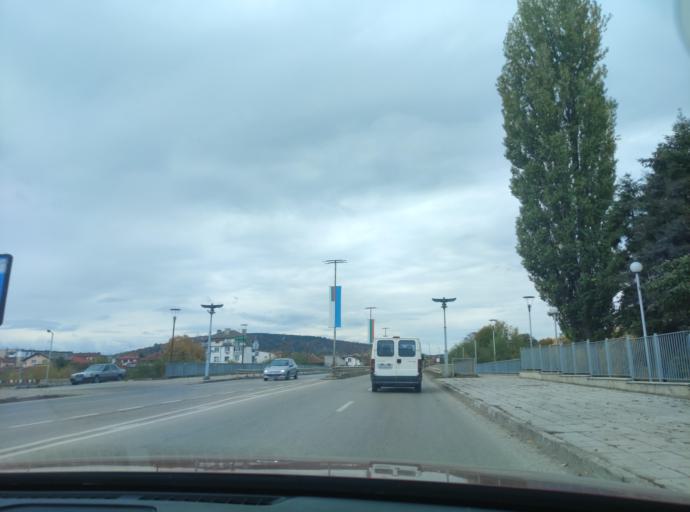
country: BG
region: Montana
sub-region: Obshtina Montana
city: Montana
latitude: 43.4014
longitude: 23.2318
